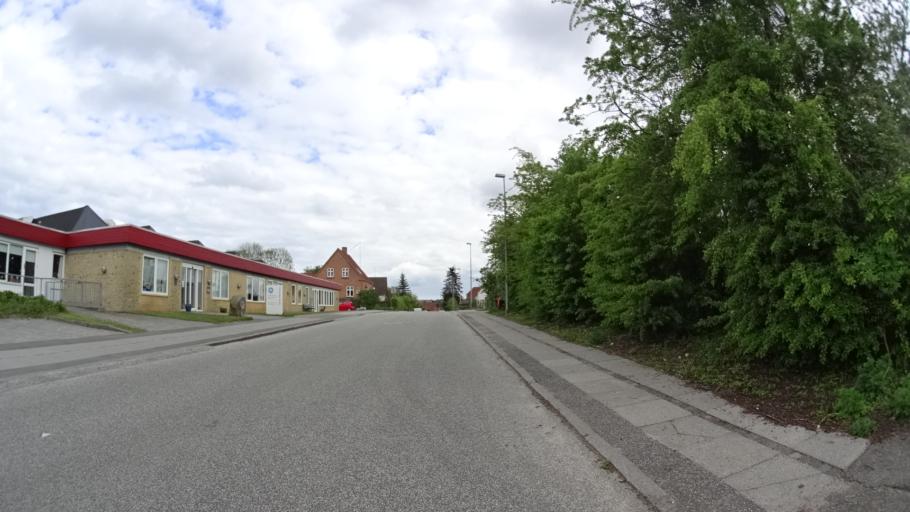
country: DK
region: Central Jutland
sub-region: Arhus Kommune
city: Stavtrup
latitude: 56.1306
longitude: 10.1487
